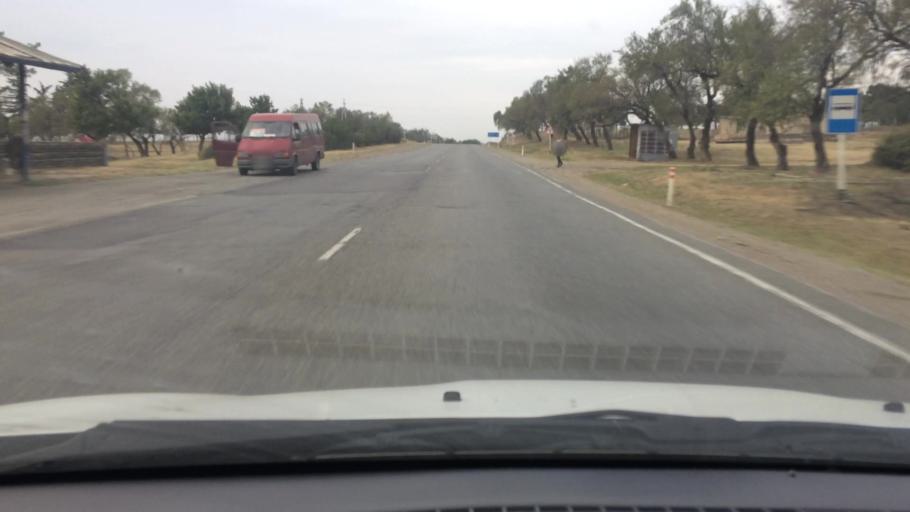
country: GE
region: T'bilisi
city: Tbilisi
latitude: 41.6395
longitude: 44.8317
